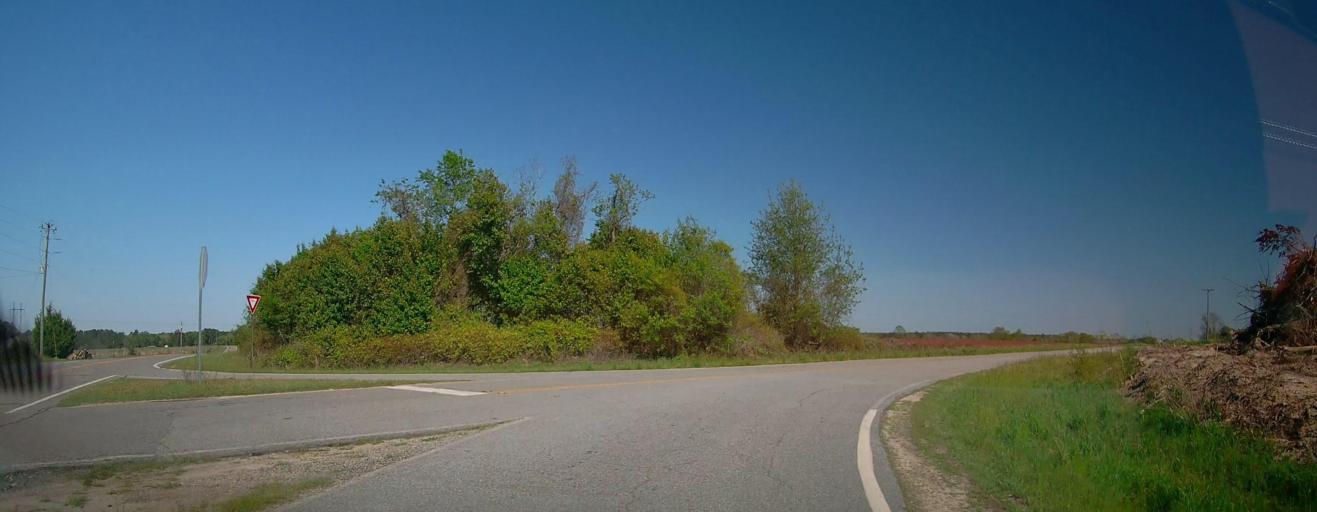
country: US
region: Georgia
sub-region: Pulaski County
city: Hawkinsville
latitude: 32.2486
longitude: -83.5835
